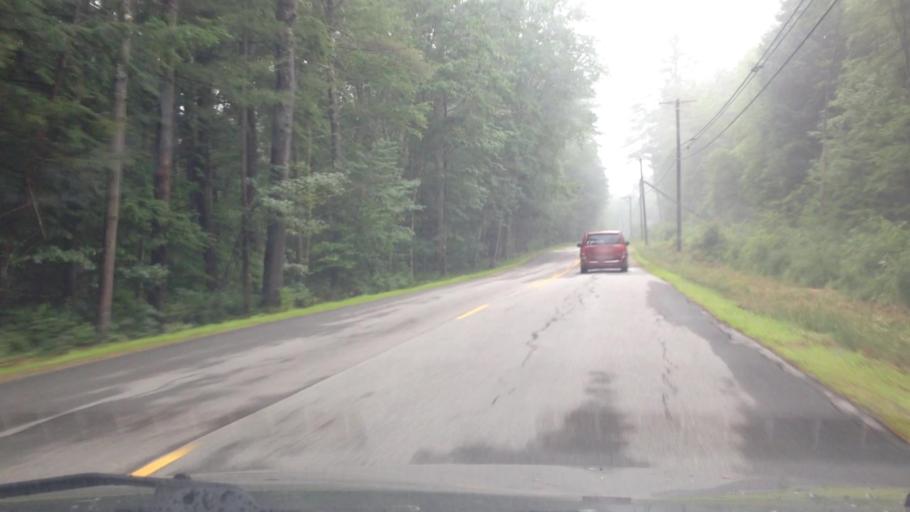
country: US
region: New Hampshire
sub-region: Cheshire County
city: Swanzey
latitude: 42.8680
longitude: -72.2385
